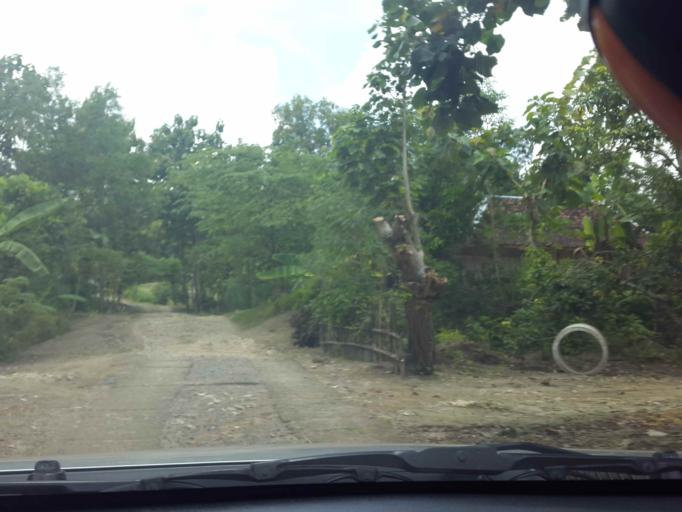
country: ID
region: Central Java
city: Sragen
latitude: -7.2987
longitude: 110.9772
